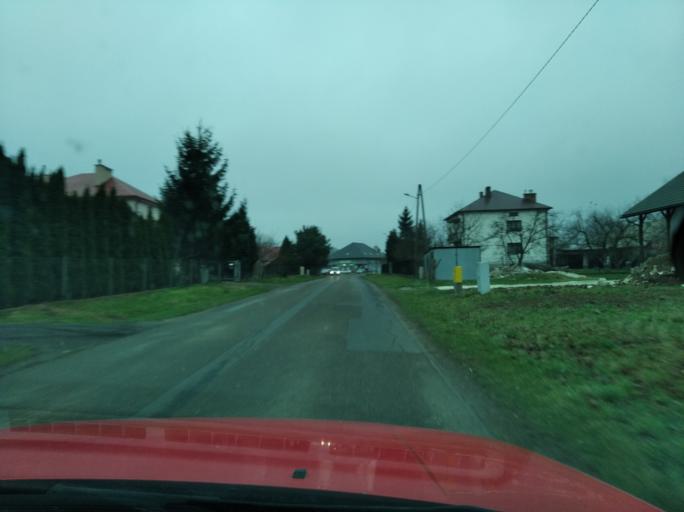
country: PL
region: Subcarpathian Voivodeship
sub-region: Powiat przeworski
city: Rozborz
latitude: 50.0626
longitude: 22.5283
